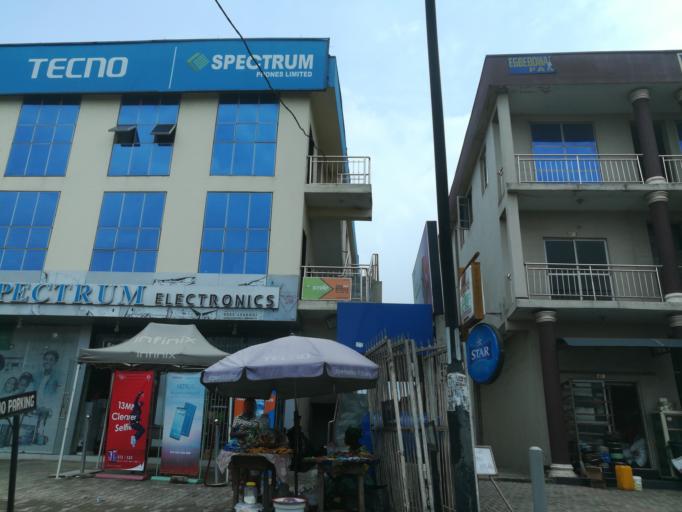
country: NG
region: Lagos
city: Agege
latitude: 6.6242
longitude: 3.3238
